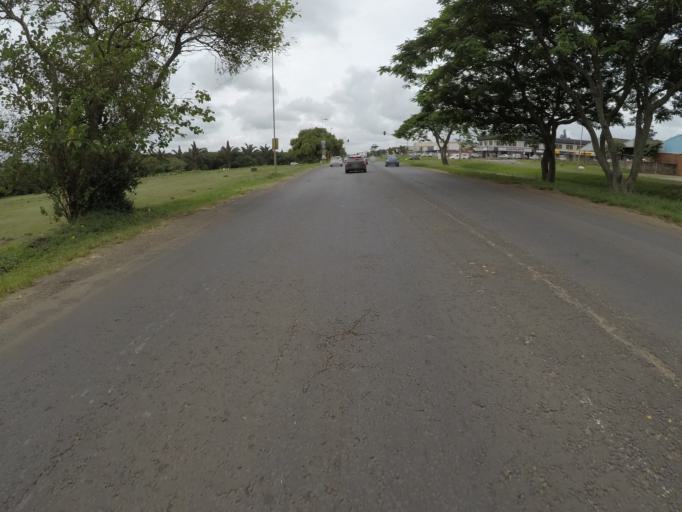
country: ZA
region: KwaZulu-Natal
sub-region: uThungulu District Municipality
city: Empangeni
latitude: -28.7694
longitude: 31.9036
